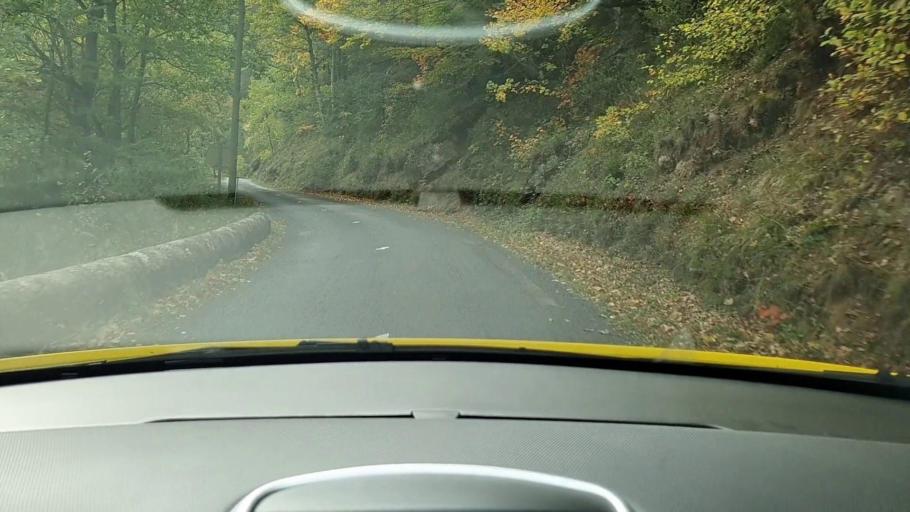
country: FR
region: Languedoc-Roussillon
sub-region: Departement de la Lozere
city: Meyrueis
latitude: 44.0925
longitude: 3.4023
